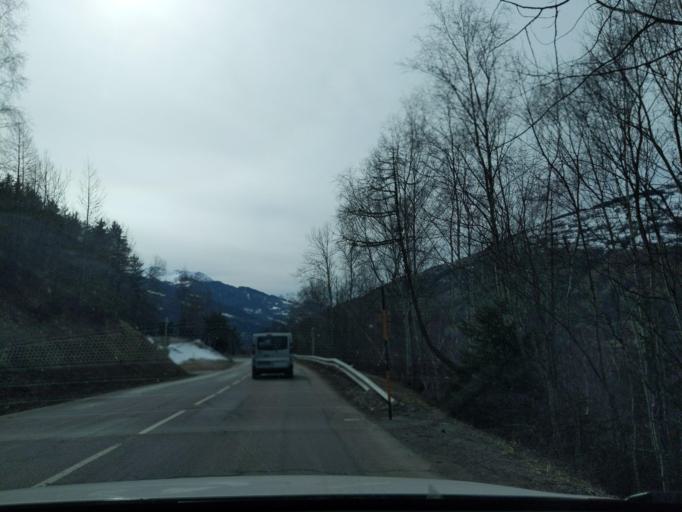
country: FR
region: Rhone-Alpes
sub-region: Departement de la Savoie
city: Bourg-Saint-Maurice
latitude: 45.5995
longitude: 6.7706
